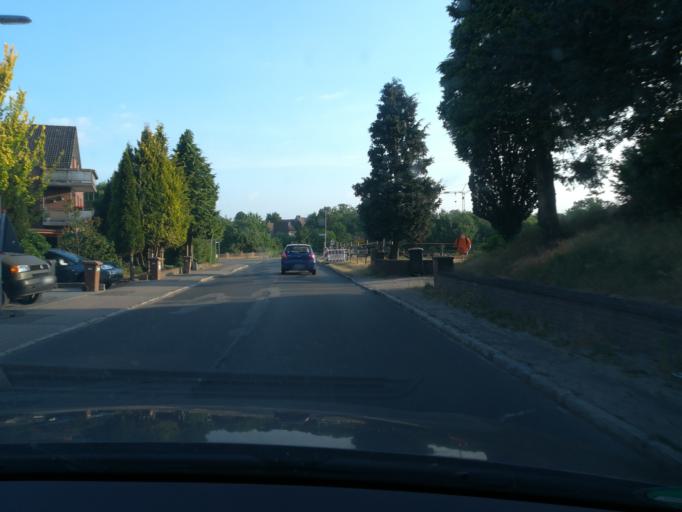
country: DE
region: Schleswig-Holstein
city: Grossensee
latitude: 53.6127
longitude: 10.3416
